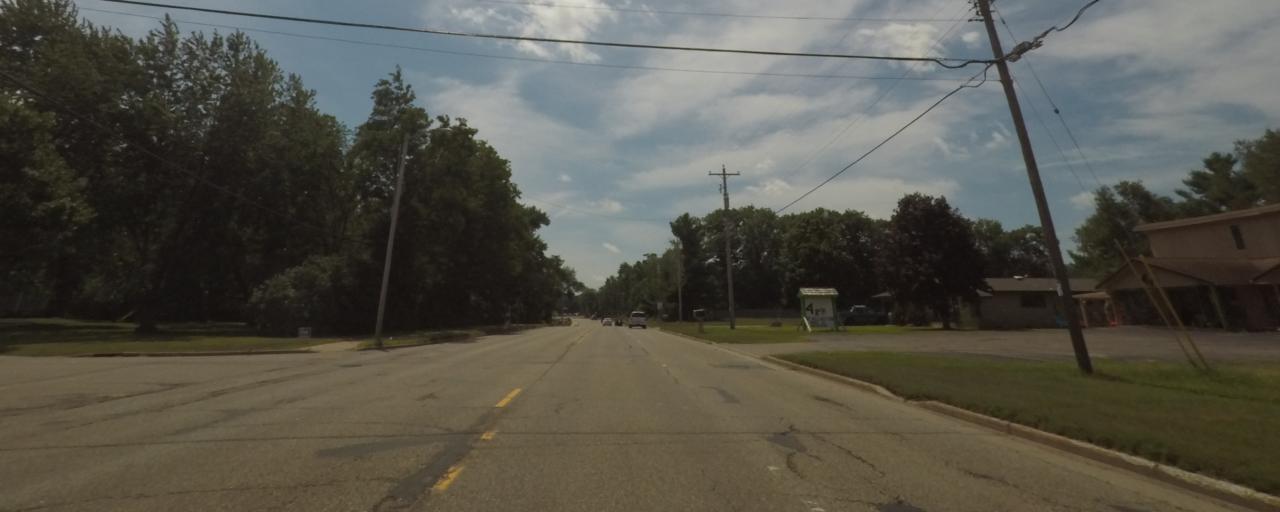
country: US
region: Wisconsin
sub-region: Portage County
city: Plover
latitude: 44.4739
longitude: -89.5476
